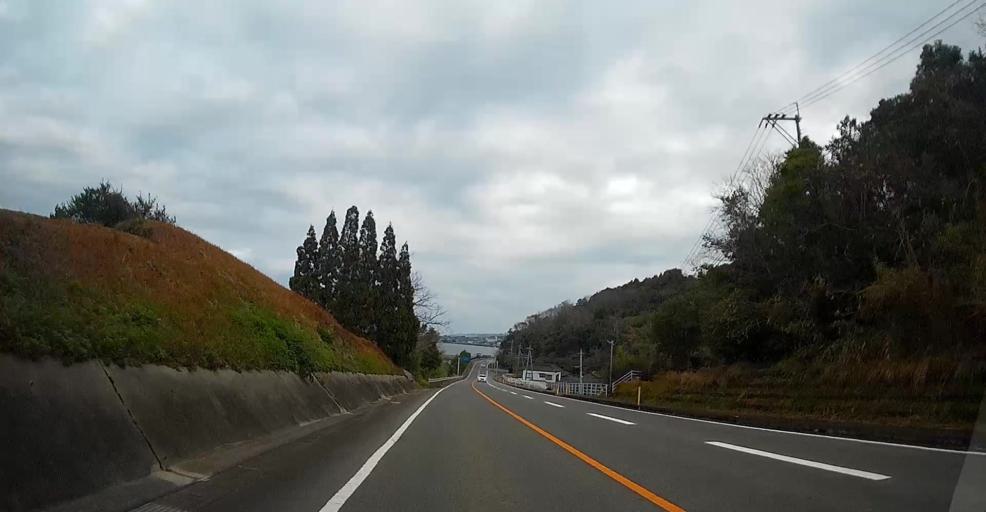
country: JP
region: Kumamoto
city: Hondo
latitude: 32.4654
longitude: 130.2418
